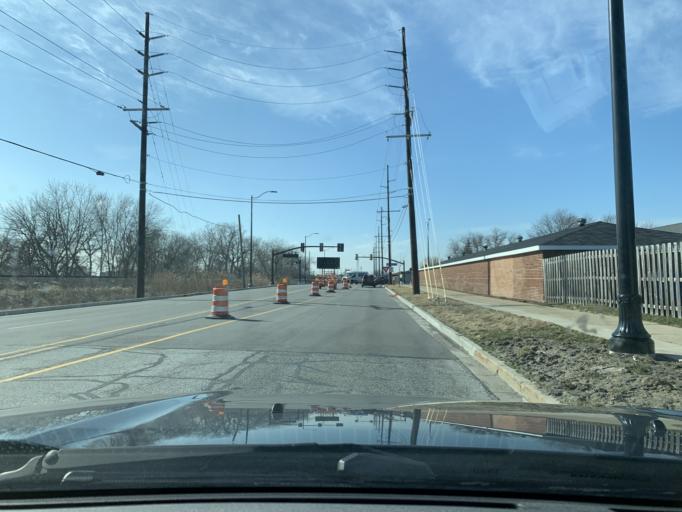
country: US
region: Indiana
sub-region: Lake County
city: Munster
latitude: 41.5391
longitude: -87.4986
